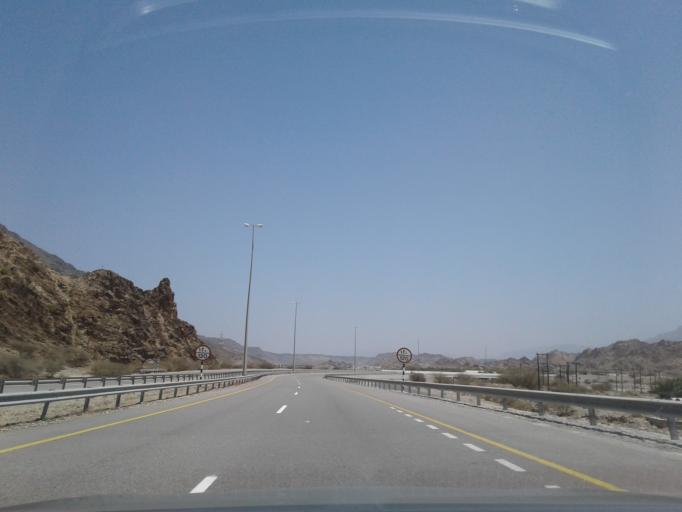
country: OM
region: Muhafazat Masqat
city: Muscat
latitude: 23.2770
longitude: 58.7536
